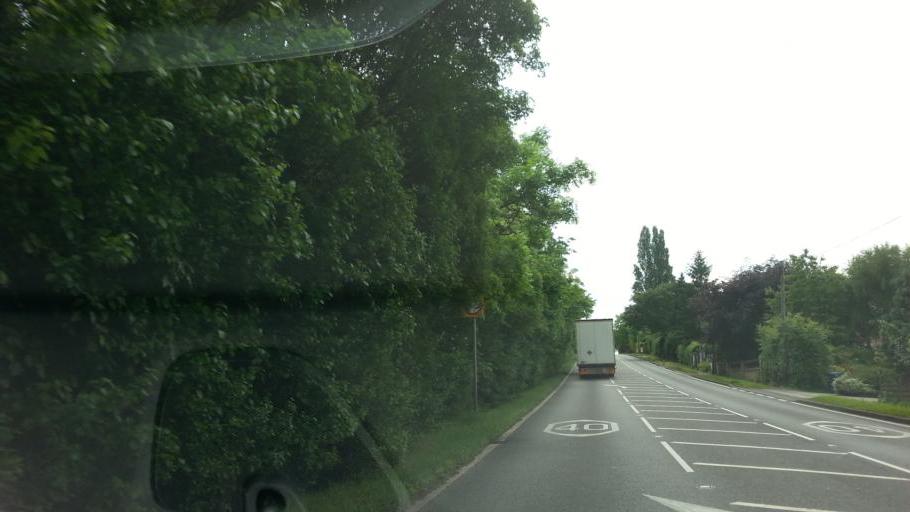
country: GB
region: England
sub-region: Nottinghamshire
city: Cotgrave
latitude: 52.8731
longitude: -1.0516
